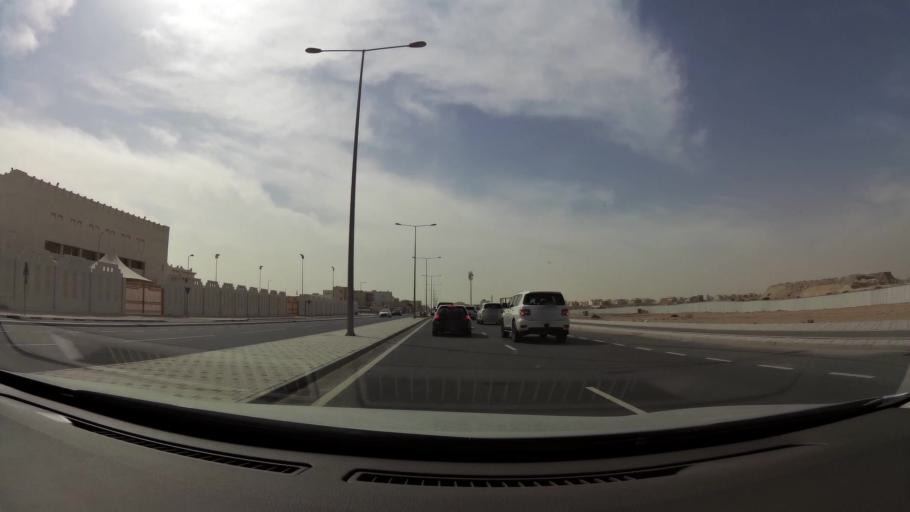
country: QA
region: Baladiyat ar Rayyan
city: Ar Rayyan
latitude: 25.3213
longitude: 51.4000
